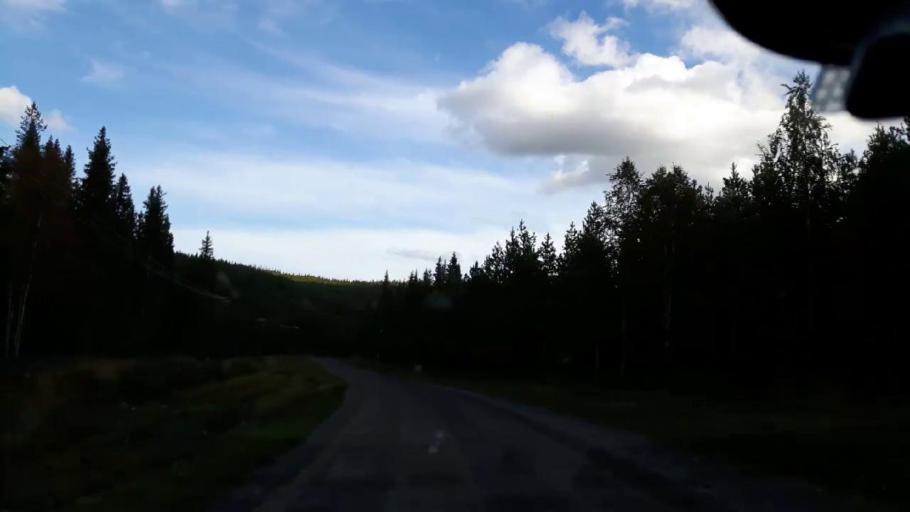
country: SE
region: Jaemtland
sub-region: Ragunda Kommun
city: Hammarstrand
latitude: 63.4220
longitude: 16.0662
